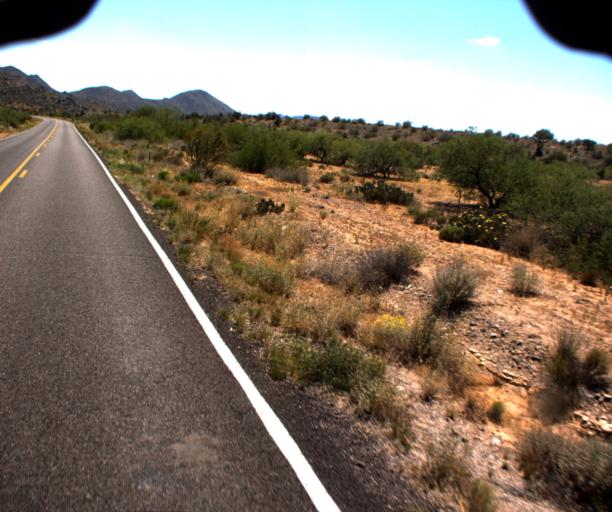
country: US
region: Arizona
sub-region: Yavapai County
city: Bagdad
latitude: 34.4958
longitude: -113.1765
